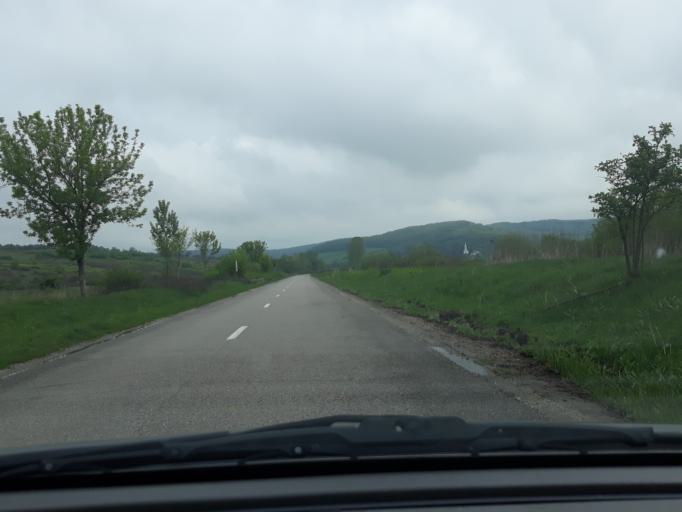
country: RO
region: Salaj
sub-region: Comuna Dobrin
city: Dobrin
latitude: 47.2940
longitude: 23.1151
